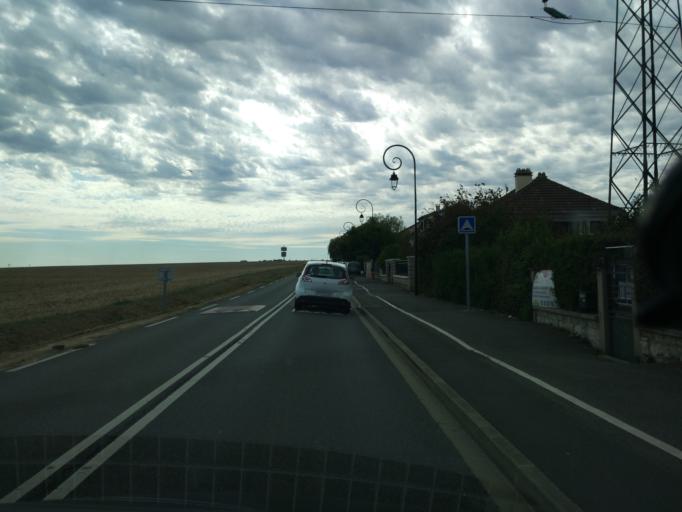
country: FR
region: Ile-de-France
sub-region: Departement de l'Essonne
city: Gometz-la-Ville
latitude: 48.6666
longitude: 2.1281
